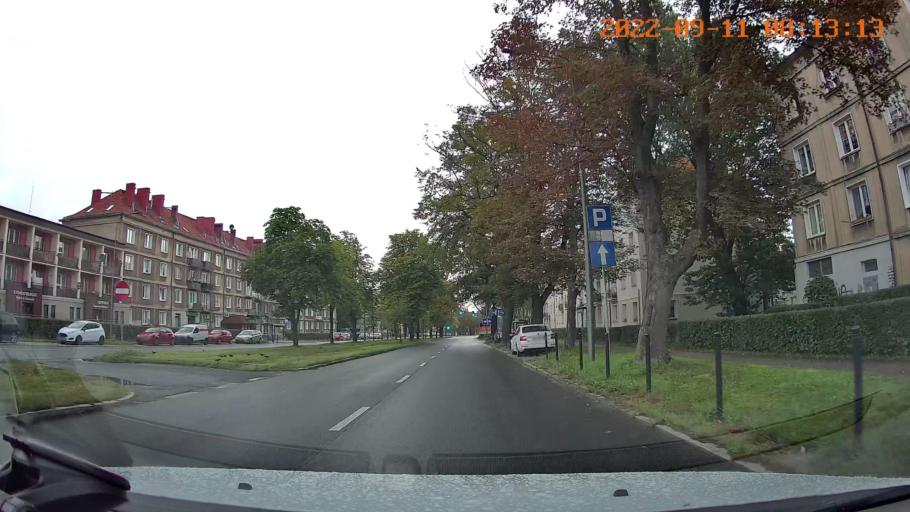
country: PL
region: Silesian Voivodeship
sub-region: Tychy
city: Tychy
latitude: 50.1183
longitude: 18.9834
